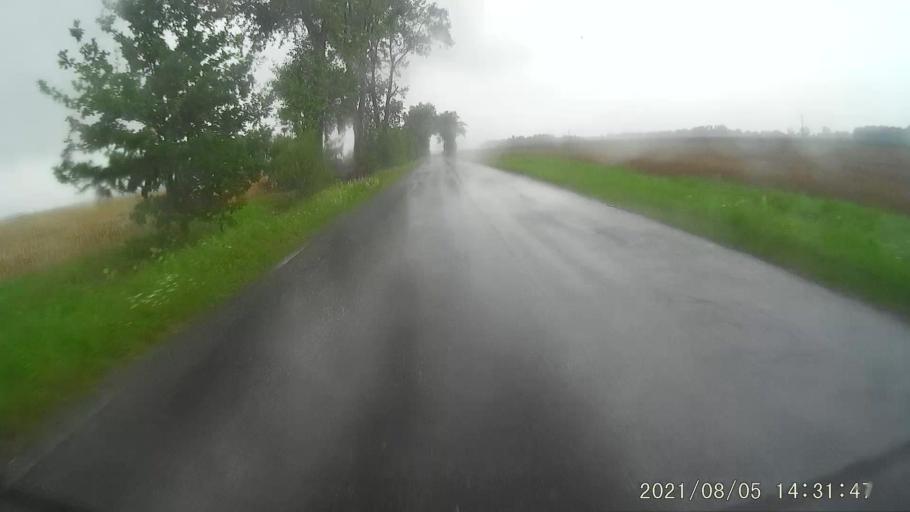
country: PL
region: Opole Voivodeship
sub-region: Powiat nyski
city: Korfantow
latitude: 50.4717
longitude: 17.5535
